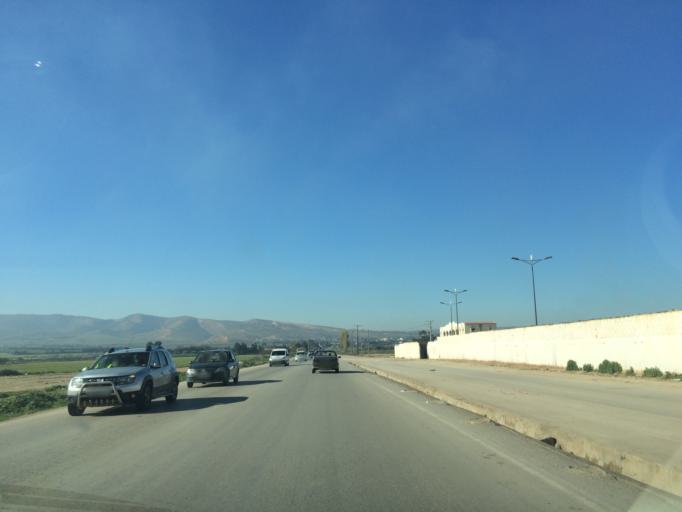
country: DZ
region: Relizane
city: Relizane
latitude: 35.8978
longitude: 0.5443
